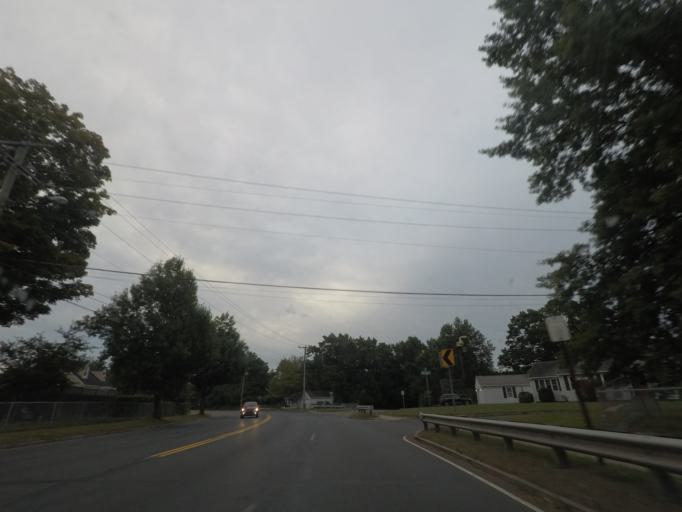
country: US
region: Massachusetts
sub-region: Hampden County
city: Ludlow
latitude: 42.1491
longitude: -72.5145
